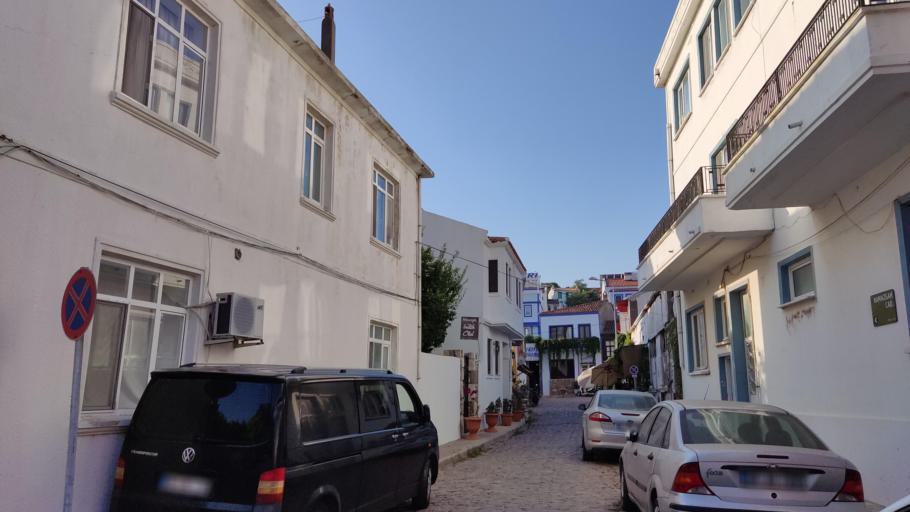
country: TR
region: Canakkale
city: Bozcaada
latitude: 39.8337
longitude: 26.0712
